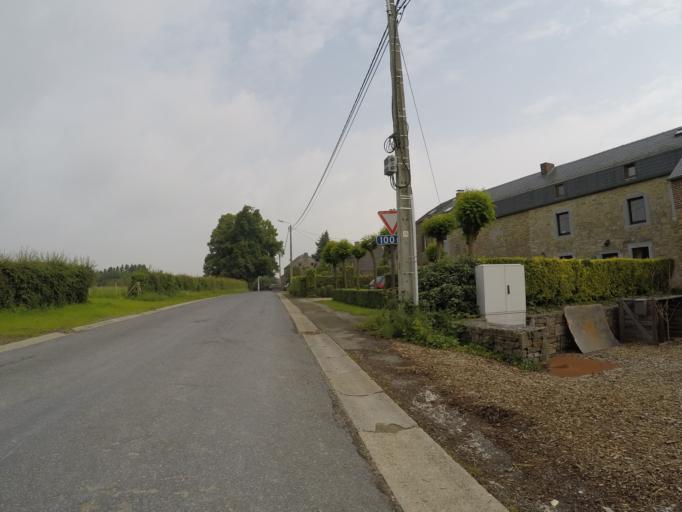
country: BE
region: Wallonia
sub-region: Province de Namur
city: Assesse
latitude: 50.3788
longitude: 4.9849
